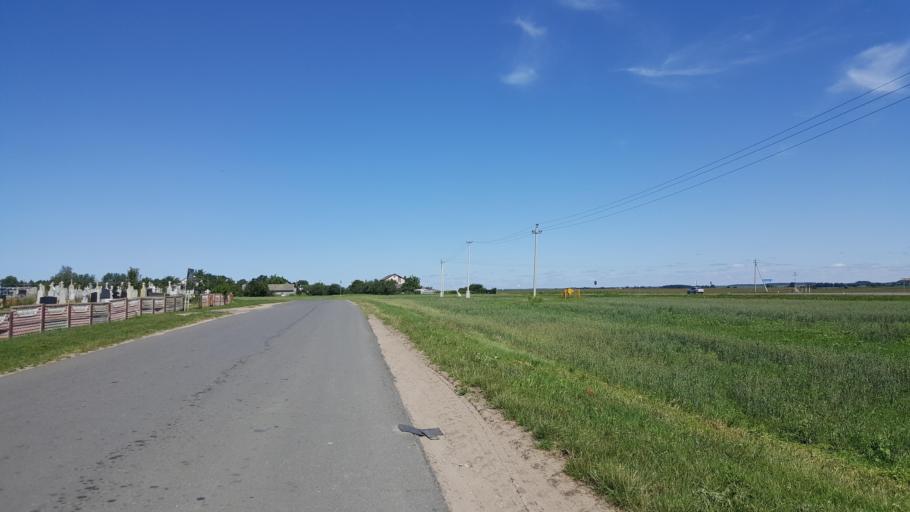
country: BY
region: Brest
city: Charnawchytsy
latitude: 52.2192
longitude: 23.7484
